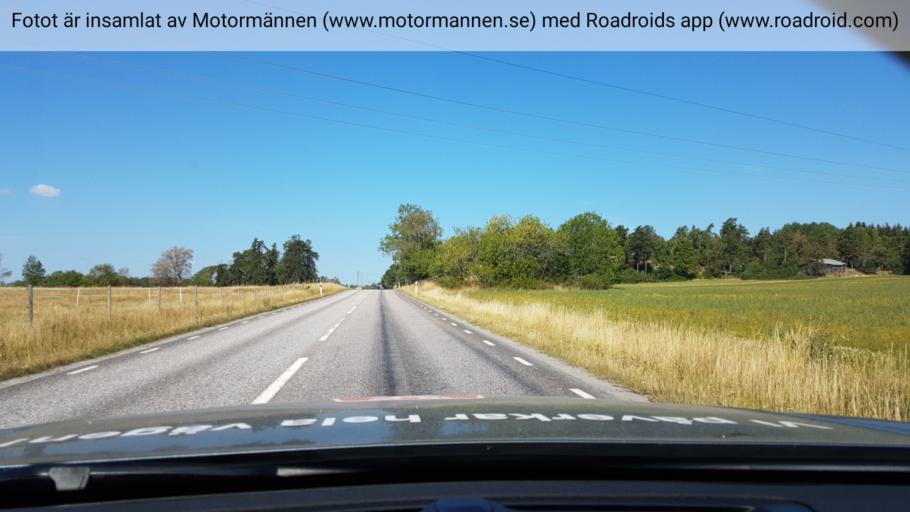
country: SE
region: Stockholm
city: Stenhamra
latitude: 59.2925
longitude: 17.6888
